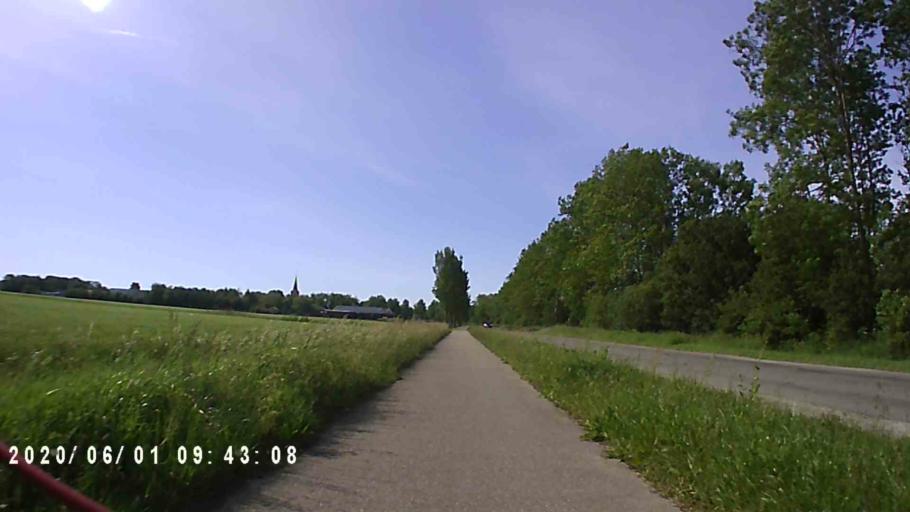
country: NL
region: Friesland
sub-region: Menameradiel
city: Berltsum
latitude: 53.2435
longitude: 5.6828
